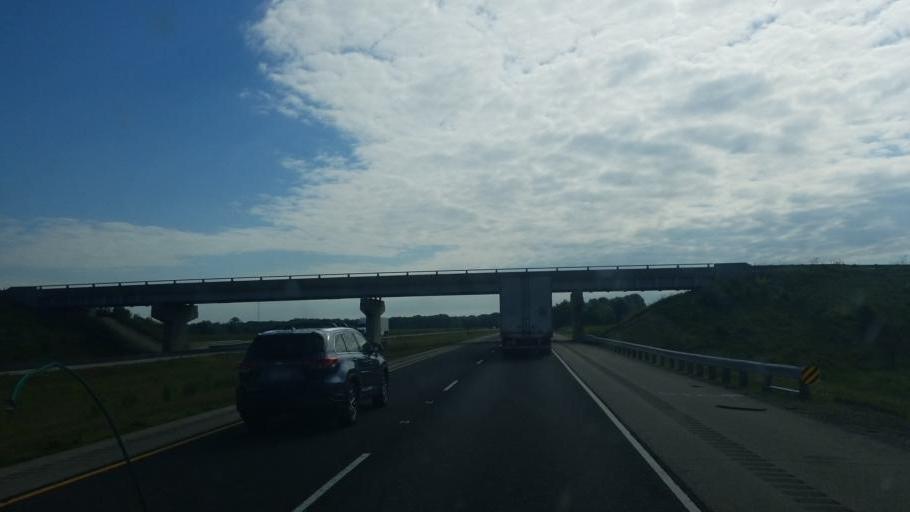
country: US
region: Illinois
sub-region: Clark County
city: Marshall
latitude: 39.3993
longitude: -87.7720
